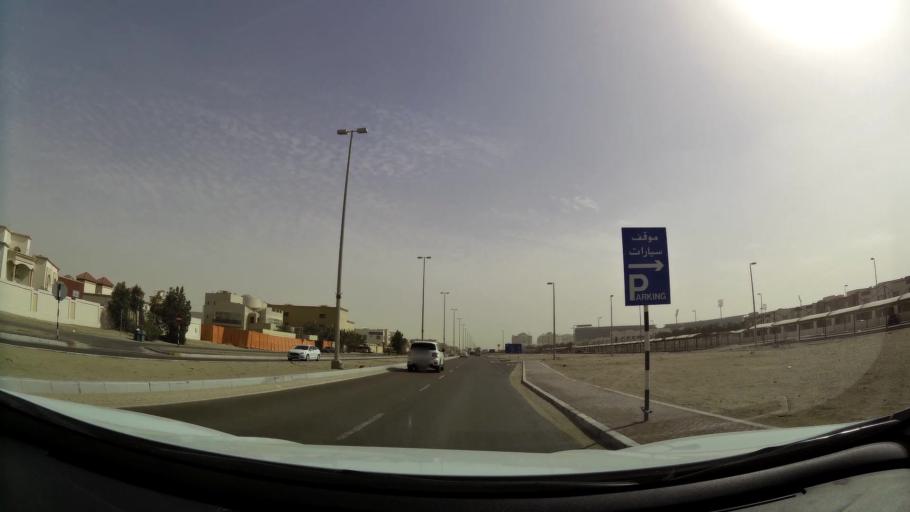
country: AE
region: Abu Dhabi
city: Abu Dhabi
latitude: 24.4135
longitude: 54.5491
